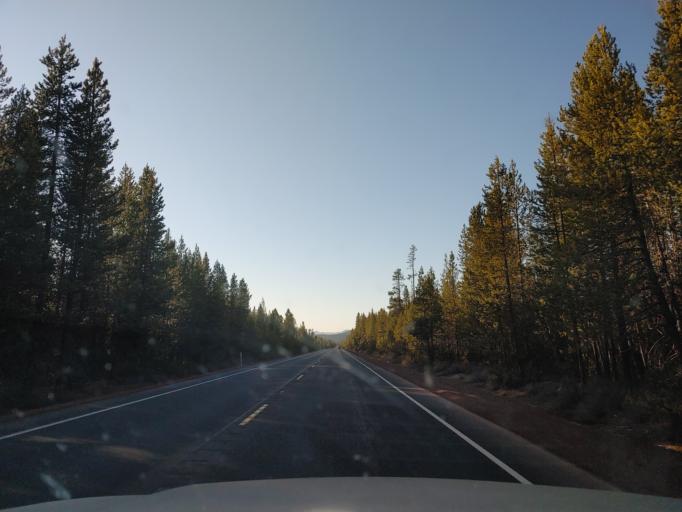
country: US
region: Oregon
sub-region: Deschutes County
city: La Pine
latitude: 43.3969
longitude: -121.8175
